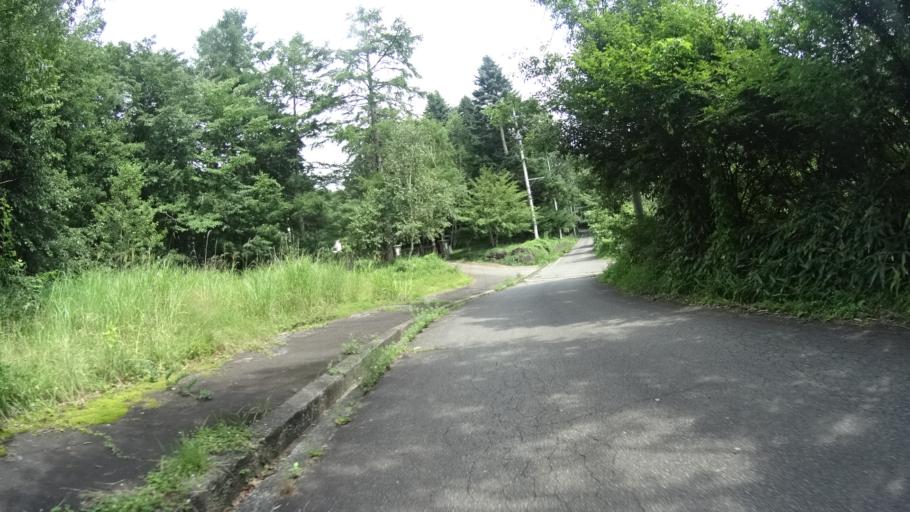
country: JP
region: Yamanashi
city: Nirasaki
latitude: 35.9041
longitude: 138.4219
